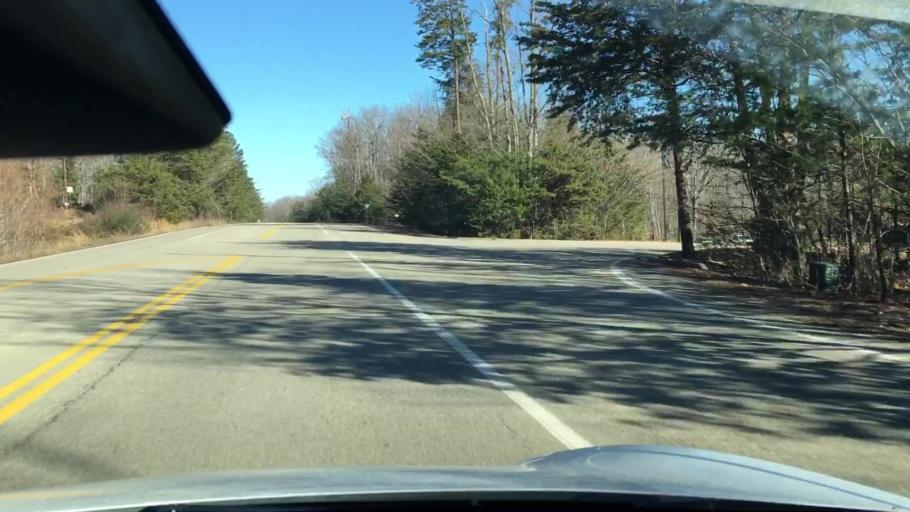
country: US
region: Virginia
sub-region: Powhatan County
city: Powhatan
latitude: 37.5230
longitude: -77.8039
